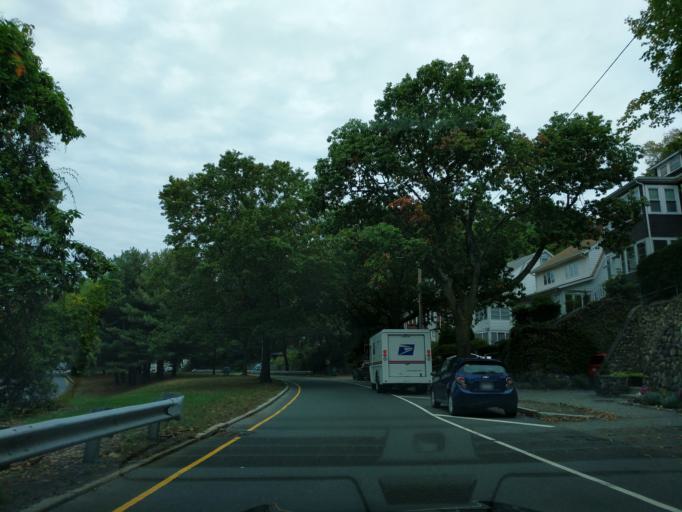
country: US
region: Massachusetts
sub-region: Middlesex County
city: Medford
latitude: 42.4336
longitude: -71.1011
